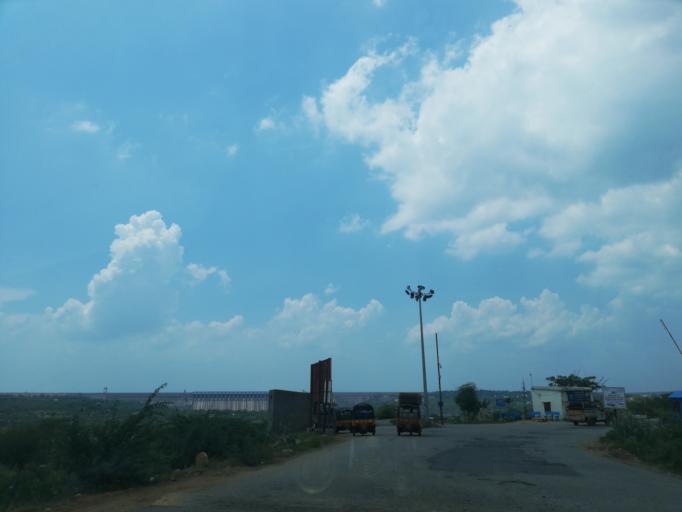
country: IN
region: Andhra Pradesh
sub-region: Guntur
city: Macherla
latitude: 16.5667
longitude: 79.3337
